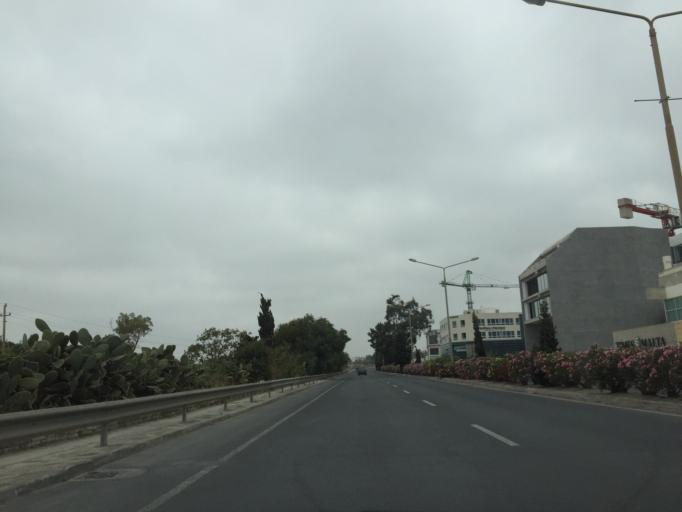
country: MT
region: Birkirkara
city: Birkirkara
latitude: 35.8891
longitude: 14.4617
